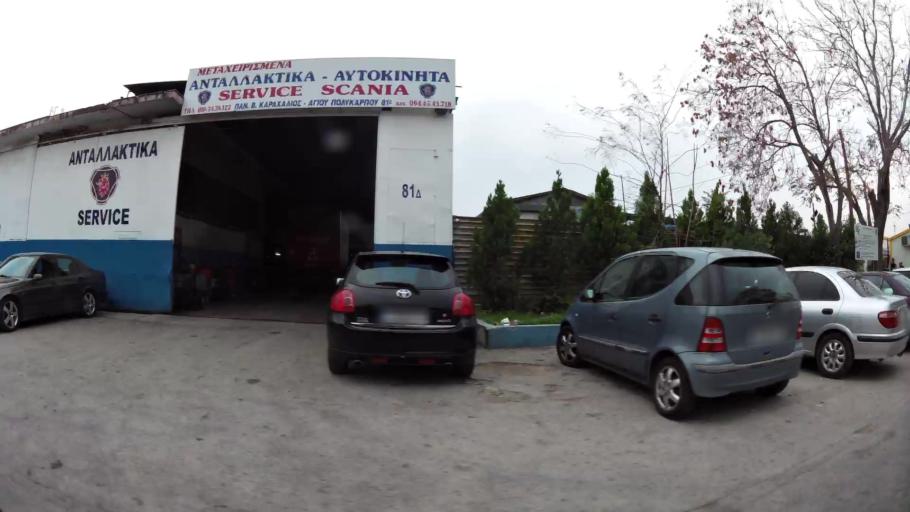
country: GR
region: Attica
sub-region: Nomarchia Athinas
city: Tavros
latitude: 37.9829
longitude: 23.6991
